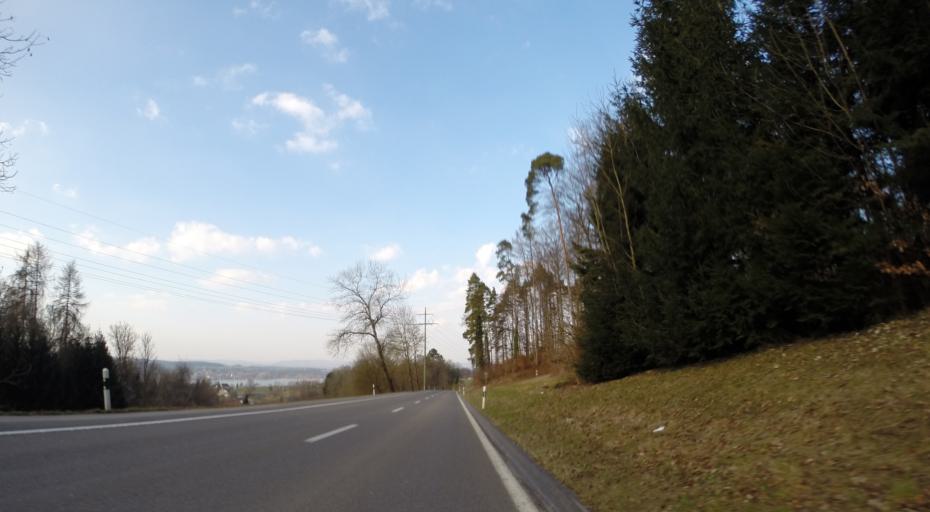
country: CH
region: Thurgau
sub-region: Frauenfeld District
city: Steckborn
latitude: 47.6552
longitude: 8.9879
